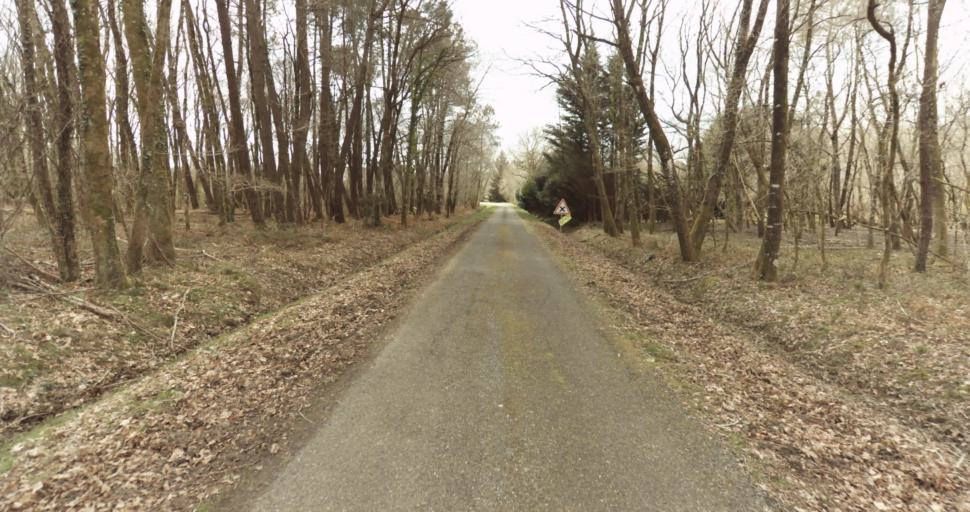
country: FR
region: Aquitaine
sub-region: Departement des Landes
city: Roquefort
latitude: 44.0762
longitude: -0.3915
